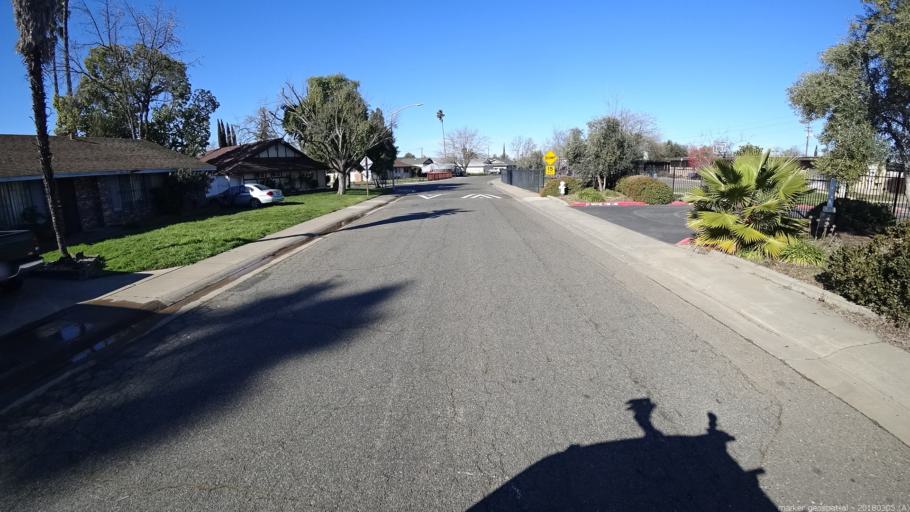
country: US
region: California
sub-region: Sacramento County
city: Florin
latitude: 38.4952
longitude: -121.4143
